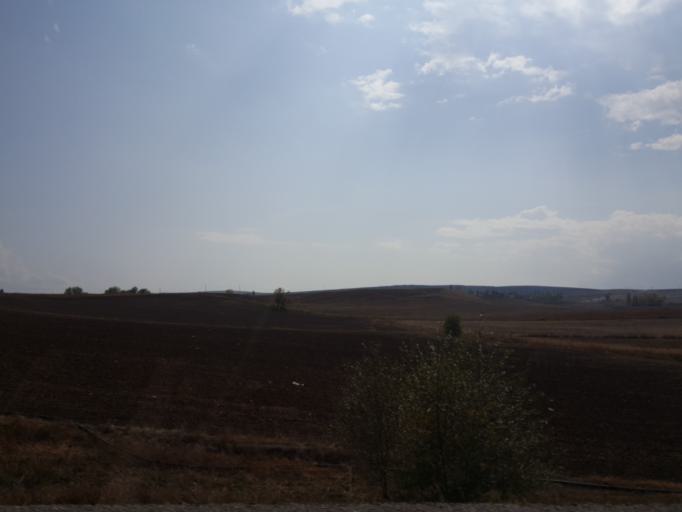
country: TR
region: Corum
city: Alaca
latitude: 40.1468
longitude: 34.8386
